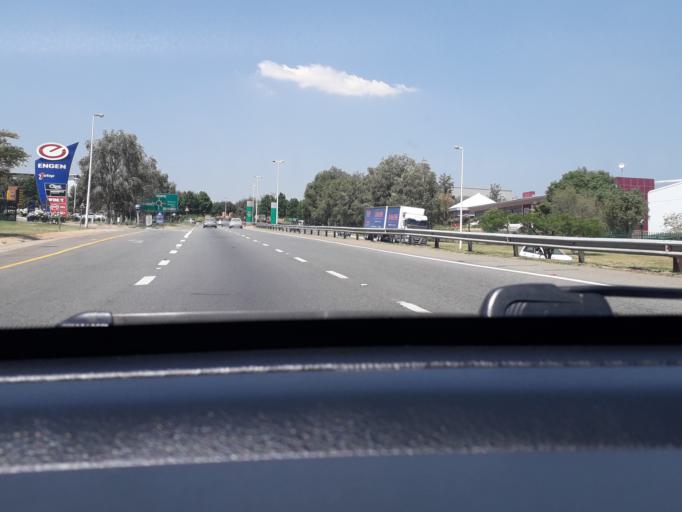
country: ZA
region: Gauteng
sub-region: City of Johannesburg Metropolitan Municipality
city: Modderfontein
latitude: -26.1162
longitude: 28.1341
